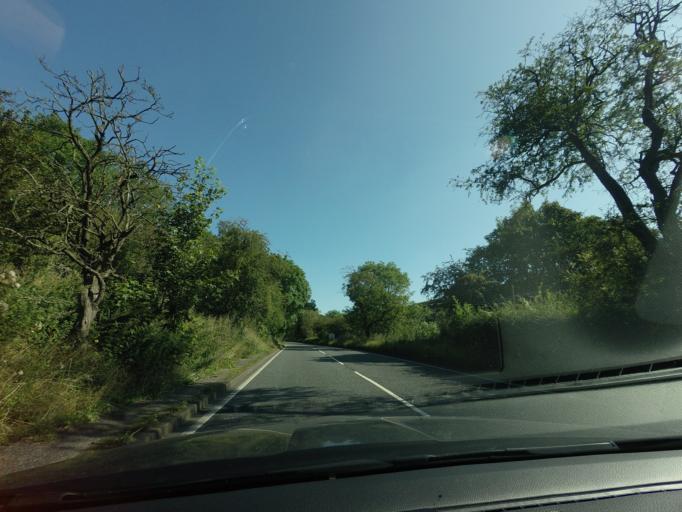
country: GB
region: England
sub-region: Derbyshire
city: Bakewell
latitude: 53.2439
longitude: -1.5802
